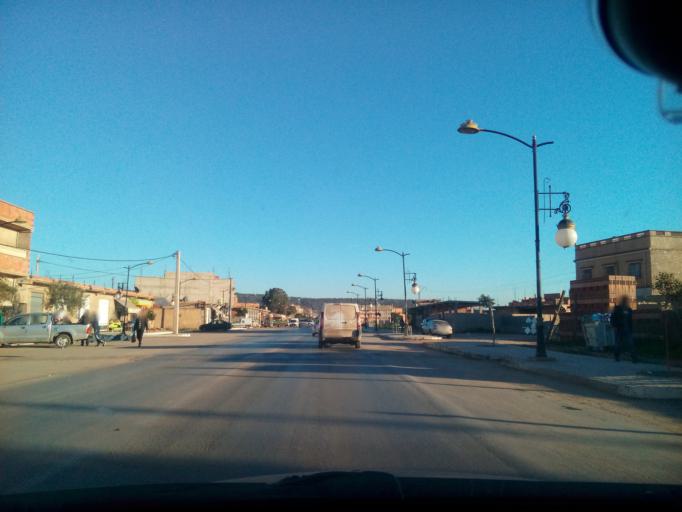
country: DZ
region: Mostaganem
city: Mostaganem
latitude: 35.7836
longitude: 0.1819
